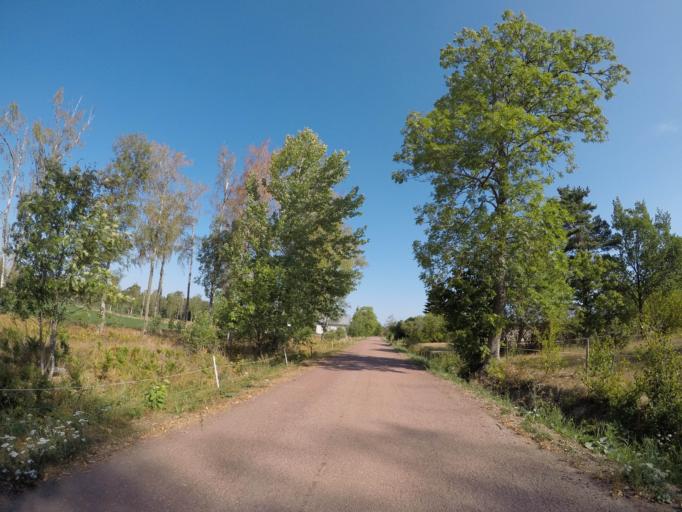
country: AX
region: Alands landsbygd
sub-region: Finstroem
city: Finstroem
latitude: 60.2792
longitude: 19.9570
